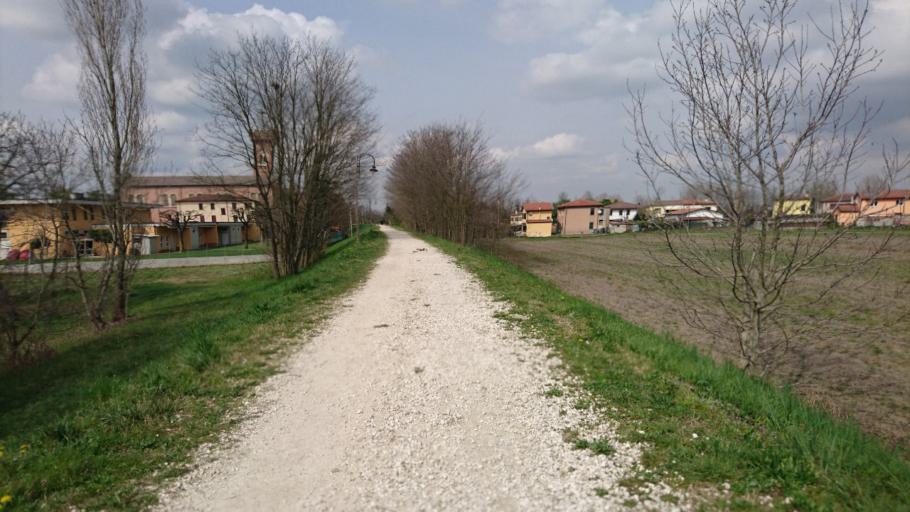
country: IT
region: Veneto
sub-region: Provincia di Padova
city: Limena
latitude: 45.4751
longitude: 11.8493
